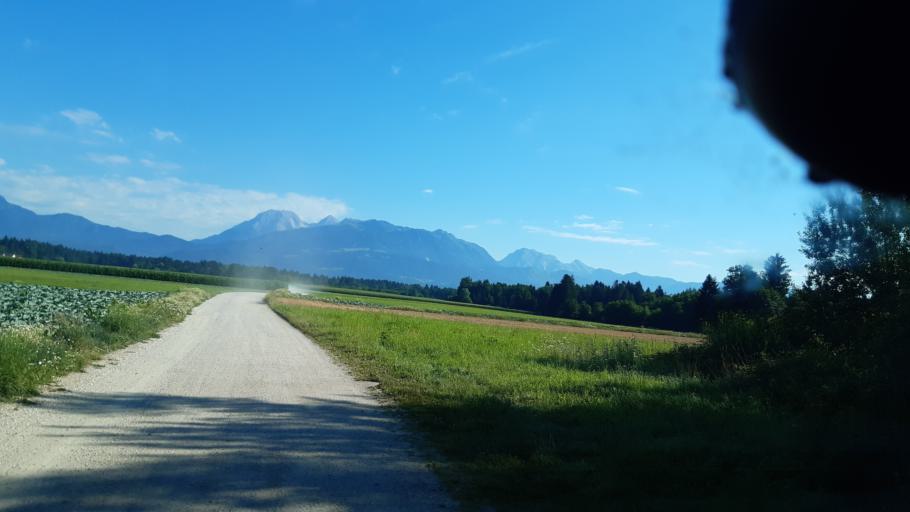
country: SI
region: Vodice
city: Vodice
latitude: 46.1833
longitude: 14.5076
